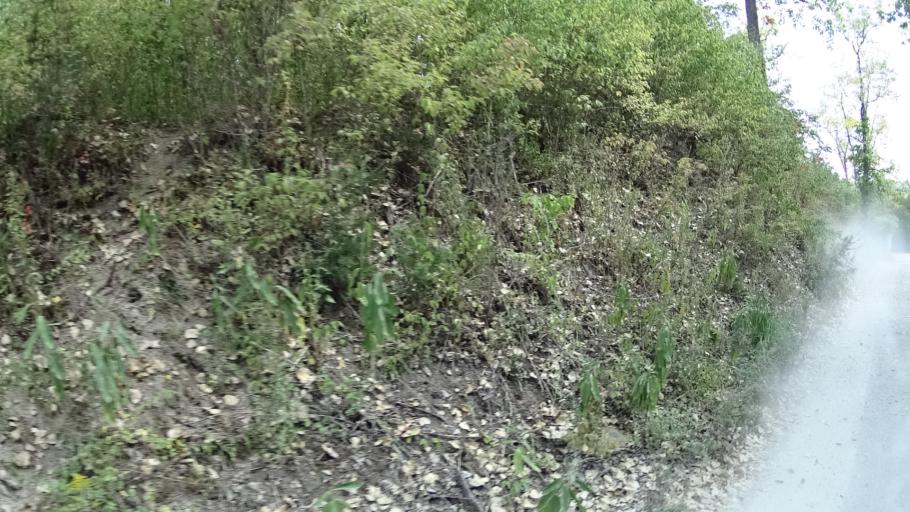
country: US
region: Ohio
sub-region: Erie County
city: Sandusky
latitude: 41.5992
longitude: -82.7185
